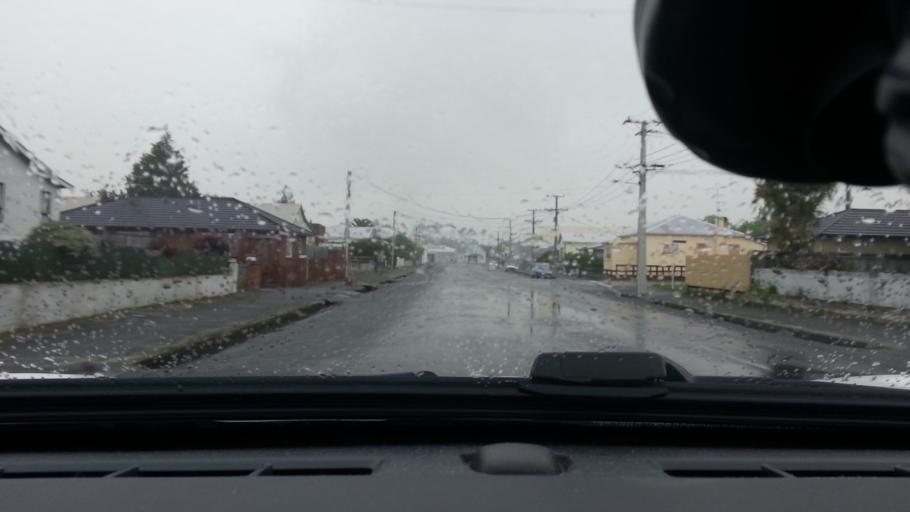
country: NZ
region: Wellington
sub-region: Masterton District
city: Masterton
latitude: -41.0242
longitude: 175.5243
